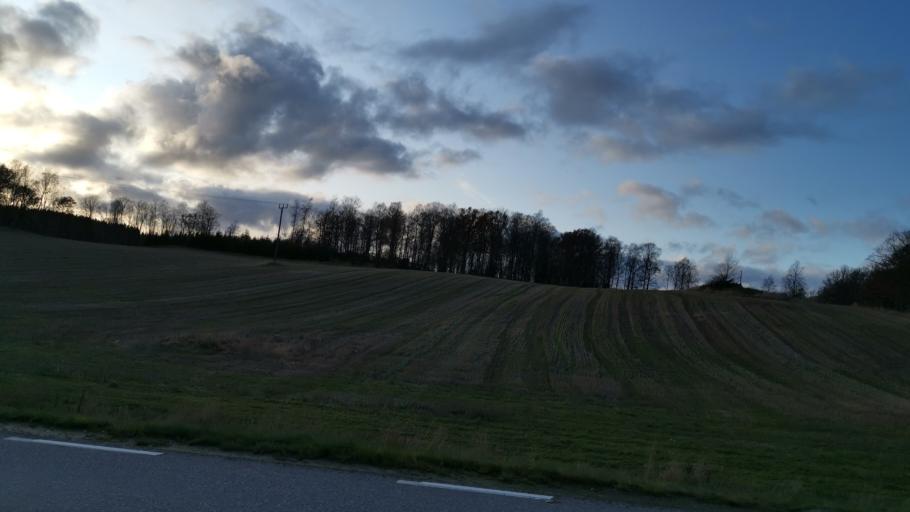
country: SE
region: Vaestra Goetaland
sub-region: Munkedals Kommun
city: Munkedal
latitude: 58.4673
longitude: 11.6589
